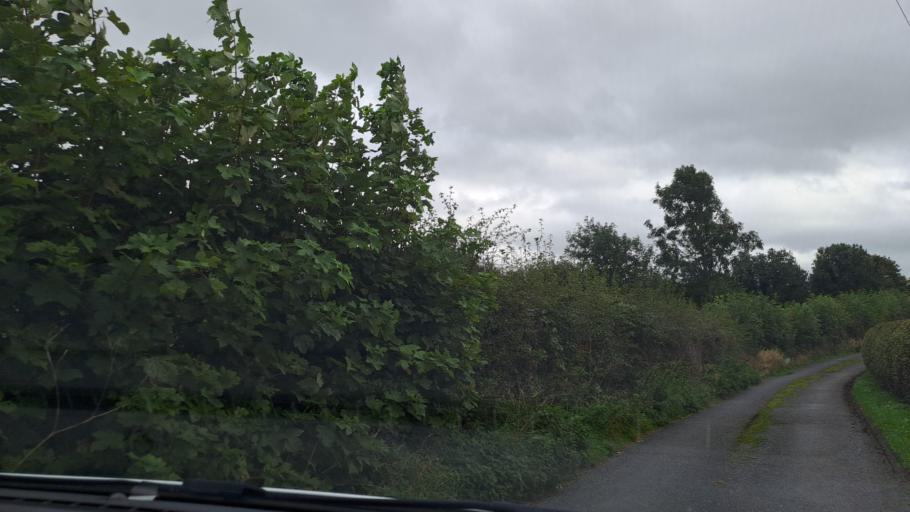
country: IE
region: Ulster
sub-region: An Cabhan
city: Bailieborough
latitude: 54.0032
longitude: -6.9055
